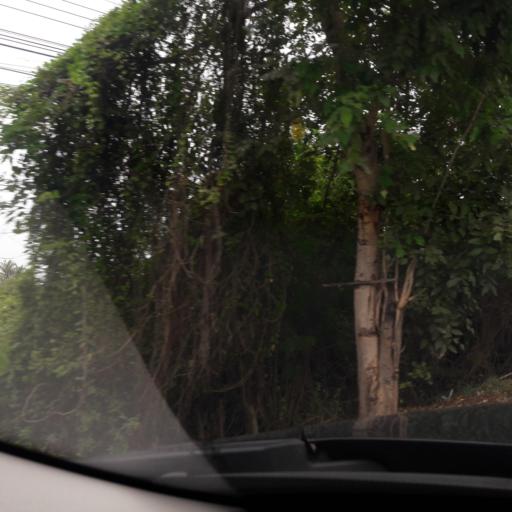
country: TH
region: Ratchaburi
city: Damnoen Saduak
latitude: 13.5720
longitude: 99.9387
